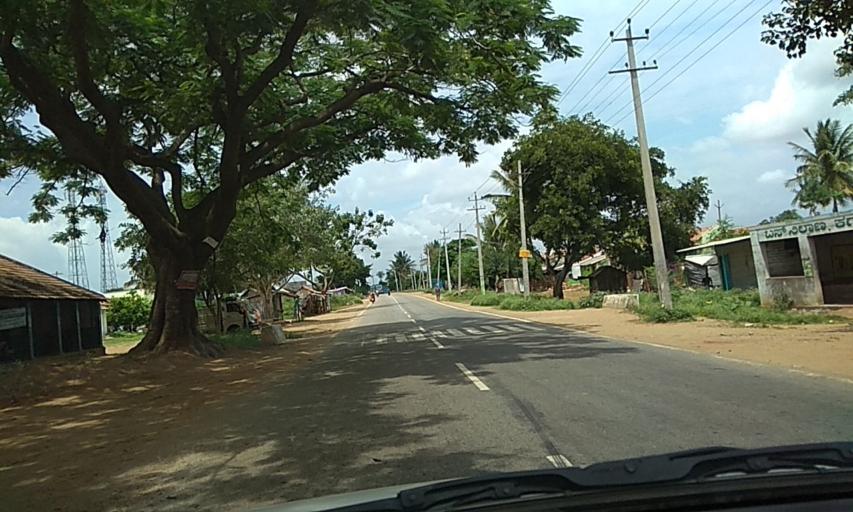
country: IN
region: Karnataka
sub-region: Chamrajnagar
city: Gundlupet
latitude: 11.8154
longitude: 76.7564
